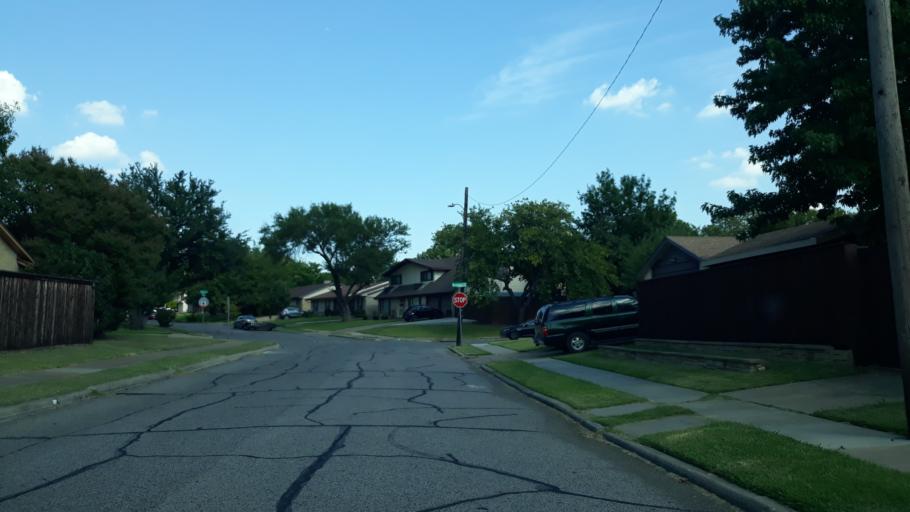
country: US
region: Texas
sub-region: Dallas County
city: Irving
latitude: 32.8444
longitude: -96.9988
